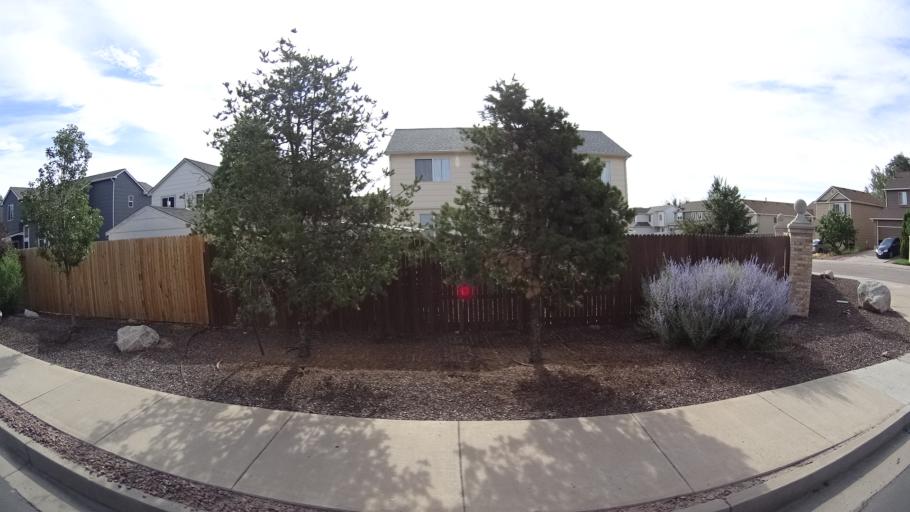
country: US
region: Colorado
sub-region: El Paso County
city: Fountain
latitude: 38.7046
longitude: -104.6968
